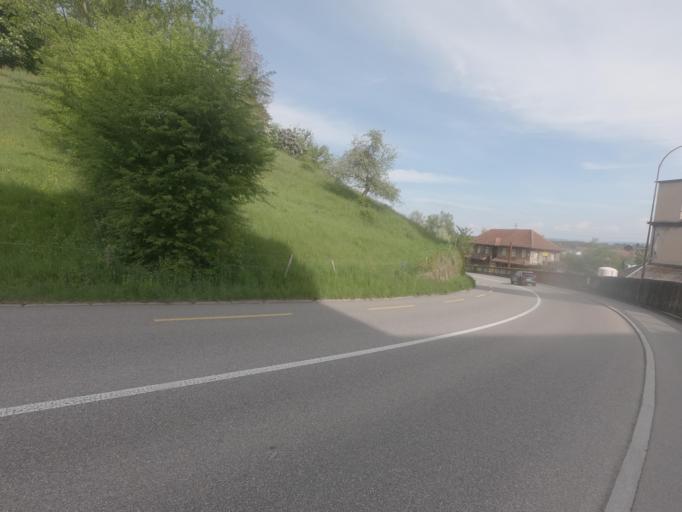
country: CH
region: Solothurn
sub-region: Bezirk Lebern
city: Riedholz
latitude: 47.2266
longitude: 7.5778
